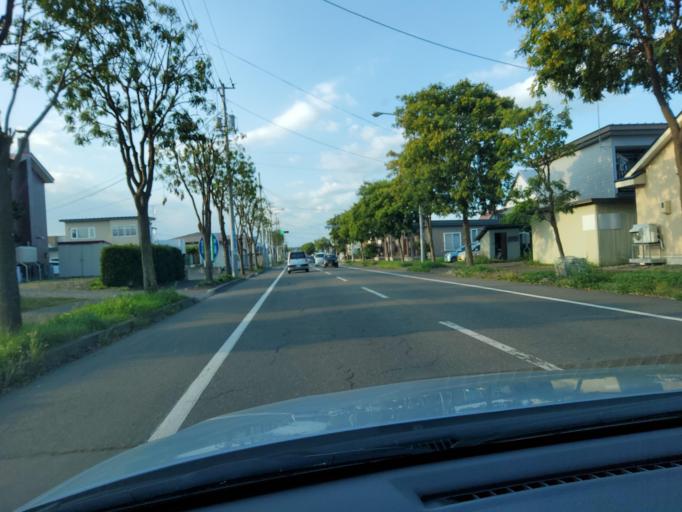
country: JP
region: Hokkaido
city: Obihiro
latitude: 42.9374
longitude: 143.1842
